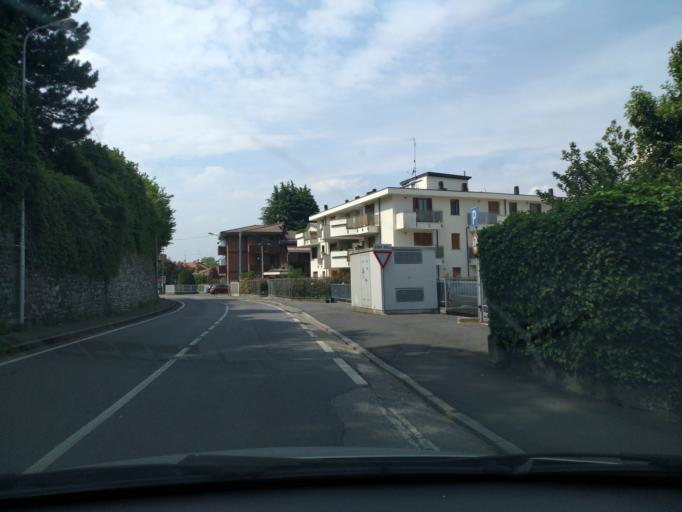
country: IT
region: Lombardy
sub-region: Provincia di Como
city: Figino Serenza
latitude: 45.7148
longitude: 9.1317
